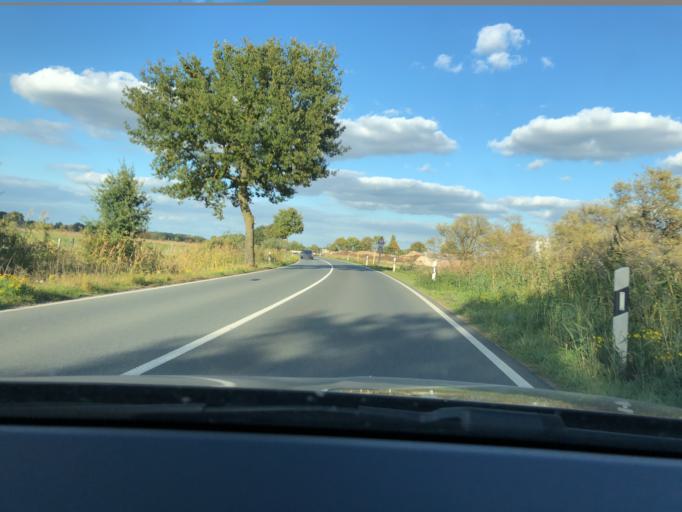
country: DE
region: Lower Saxony
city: Stuhr
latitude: 53.0215
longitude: 8.7822
